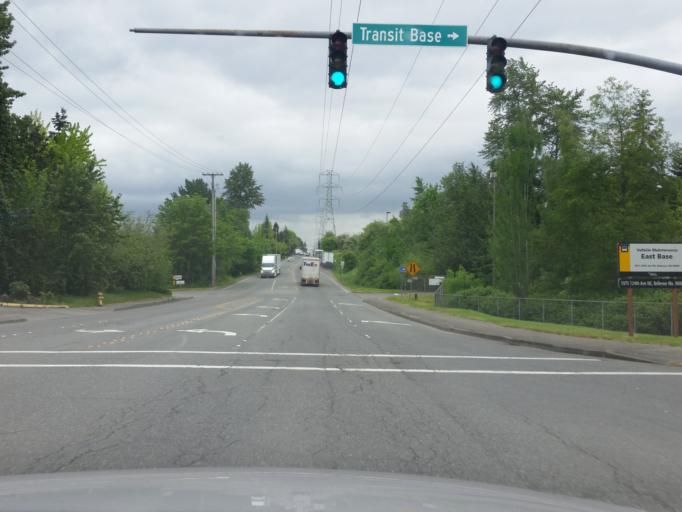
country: US
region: Washington
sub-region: King County
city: Bellevue
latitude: 47.6274
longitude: -122.1752
